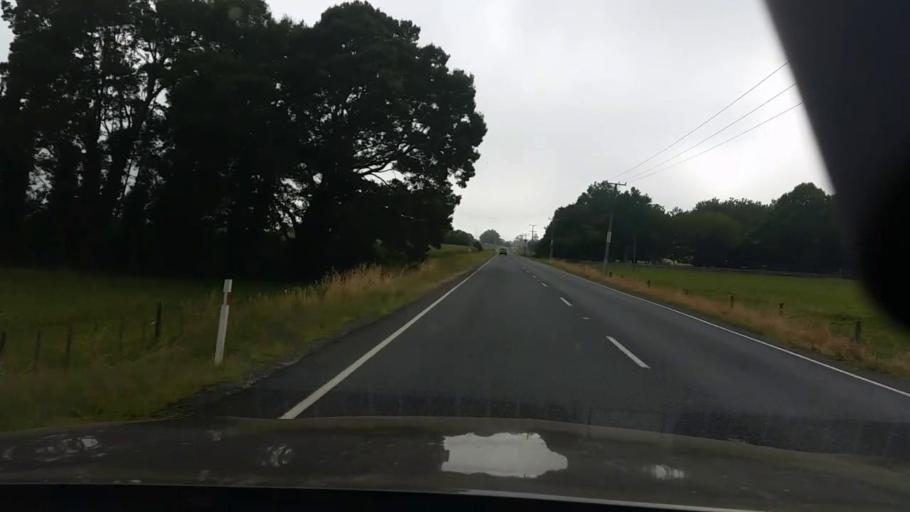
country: NZ
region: Waikato
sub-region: Hamilton City
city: Hamilton
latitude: -37.6240
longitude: 175.3263
